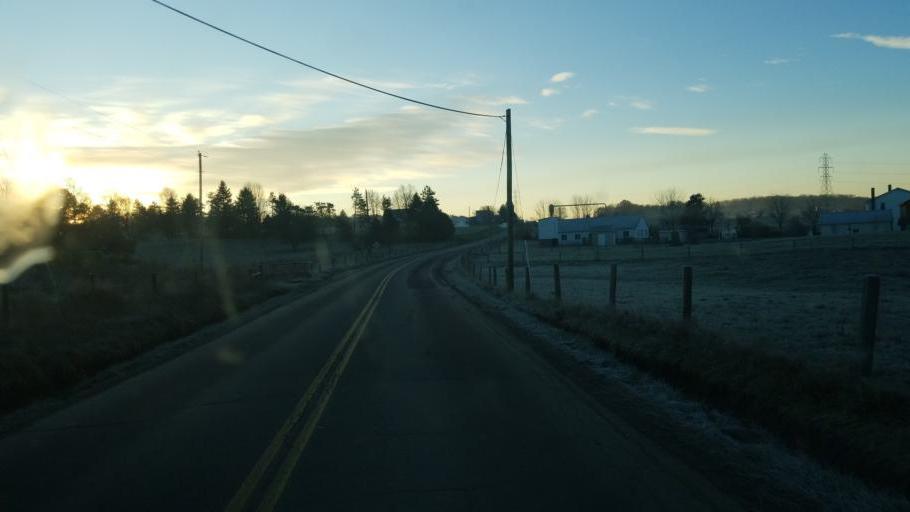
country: US
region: Ohio
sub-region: Wayne County
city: Apple Creek
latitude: 40.6607
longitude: -81.8594
